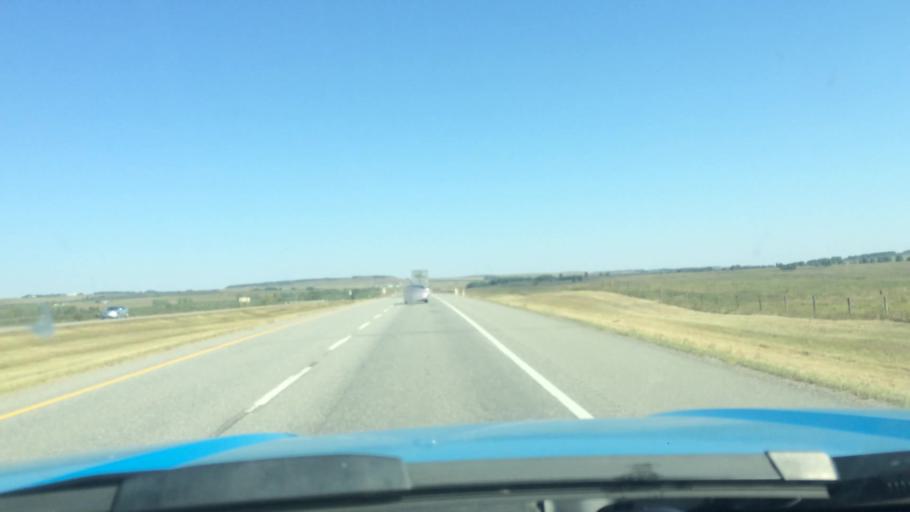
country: CA
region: Alberta
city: Cochrane
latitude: 51.0873
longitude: -114.5259
